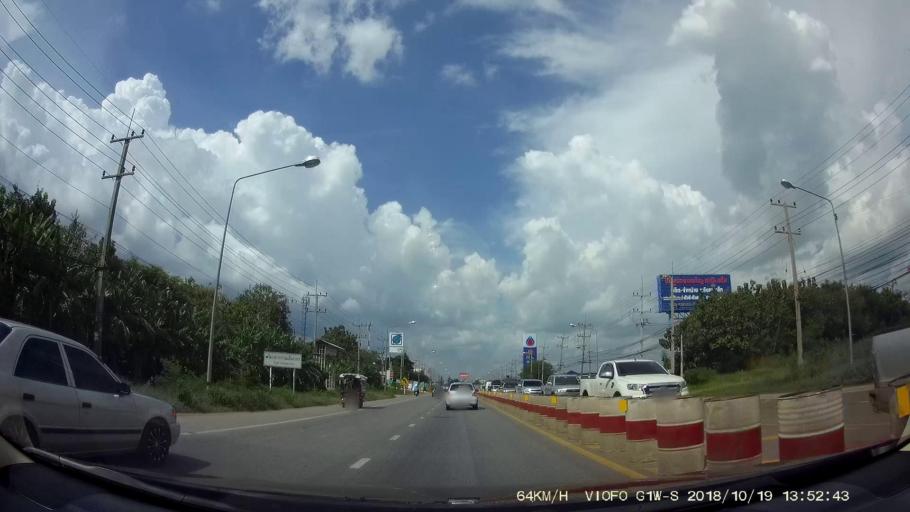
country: TH
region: Chaiyaphum
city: Chaiyaphum
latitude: 15.7702
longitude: 102.0255
